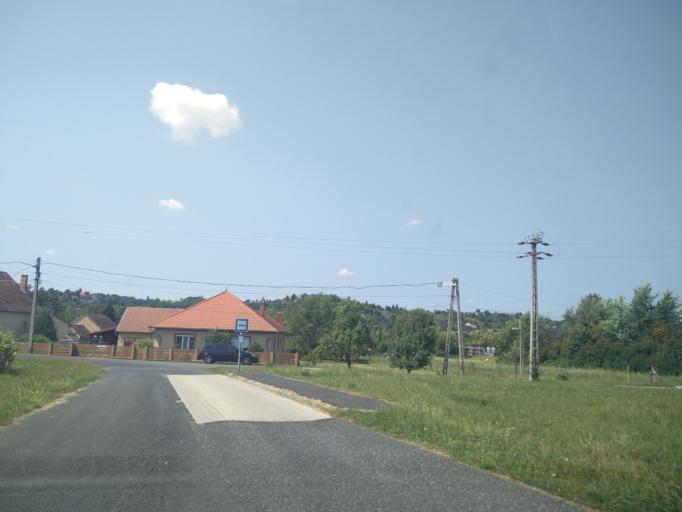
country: HU
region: Zala
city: Zalaegerszeg
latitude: 46.8156
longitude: 16.8563
